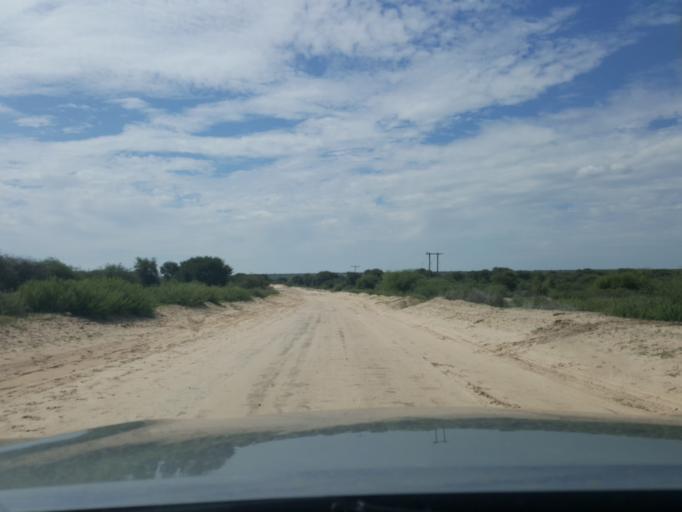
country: BW
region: Kweneng
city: Letlhakeng
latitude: -24.0682
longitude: 25.0300
